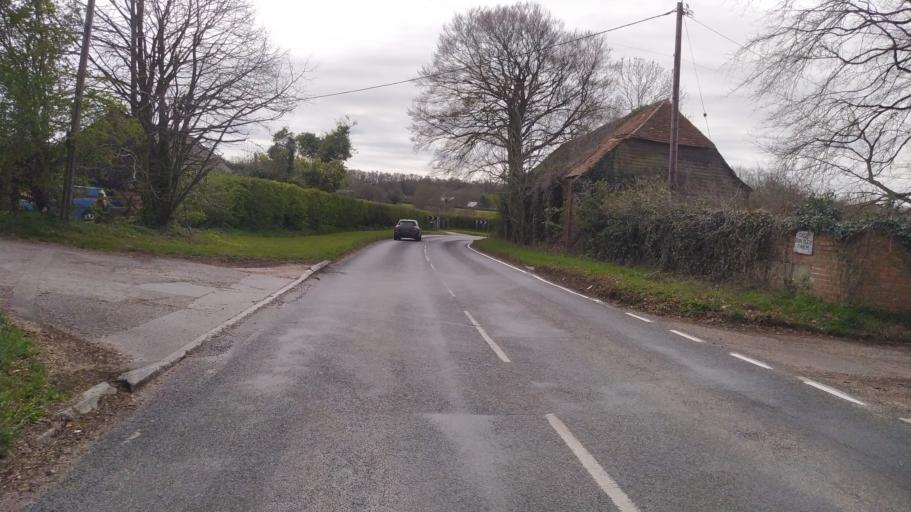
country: GB
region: England
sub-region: Hampshire
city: Wickham
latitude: 50.8782
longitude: -1.2146
